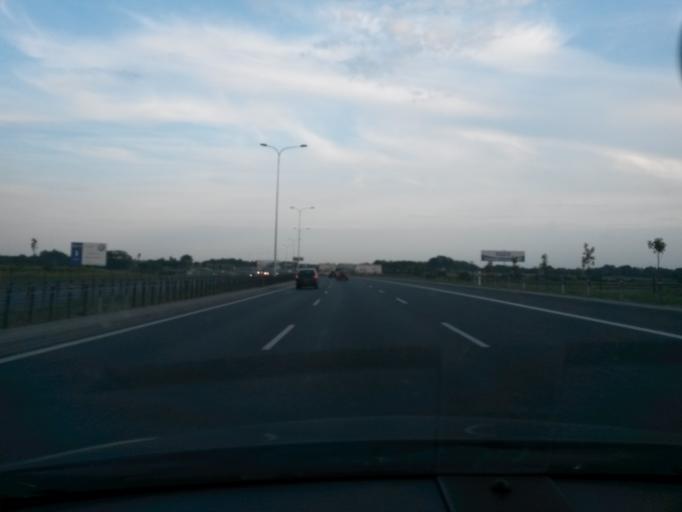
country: PL
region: Masovian Voivodeship
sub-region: Powiat pruszkowski
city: Rybie
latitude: 52.1463
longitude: 20.9640
